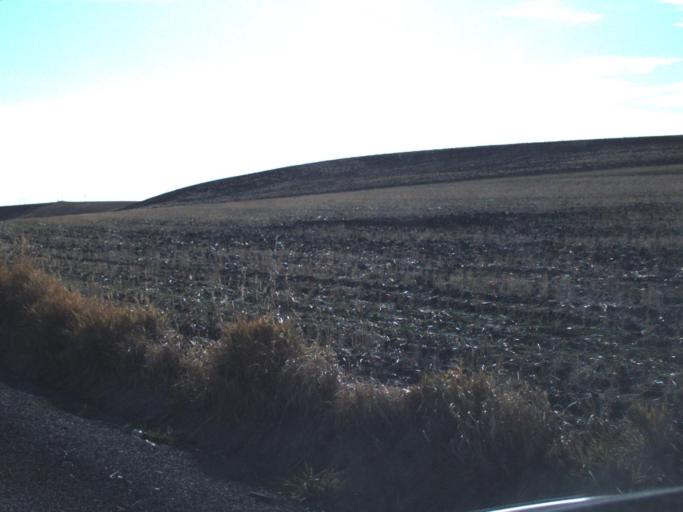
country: US
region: Washington
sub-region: Whitman County
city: Pullman
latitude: 46.9276
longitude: -117.1093
